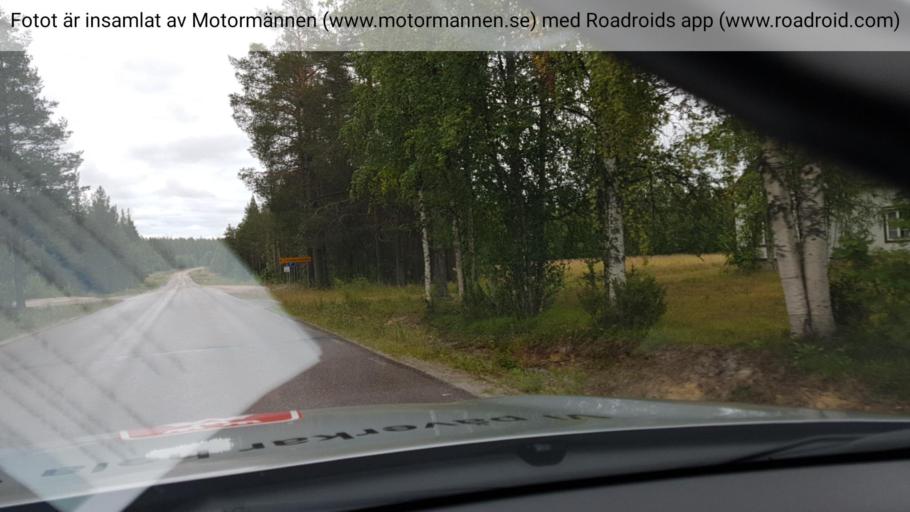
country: SE
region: Norrbotten
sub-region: Overkalix Kommun
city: OEverkalix
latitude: 67.0640
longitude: 22.2526
